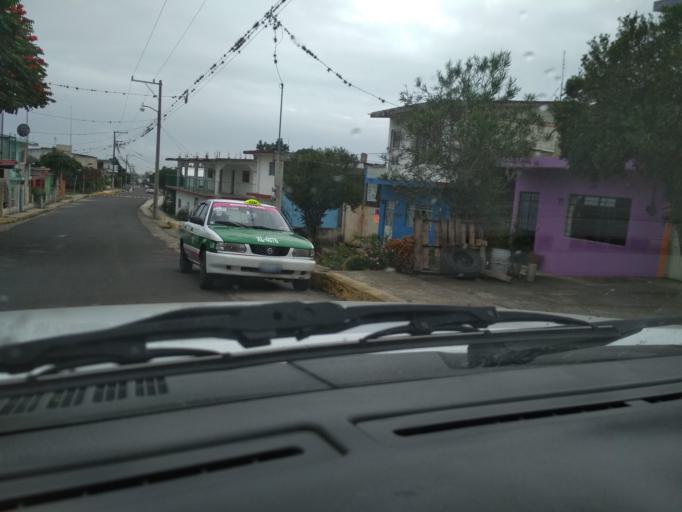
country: MX
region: Veracruz
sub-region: Emiliano Zapata
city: Dos Rios
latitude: 19.5252
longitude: -96.7998
